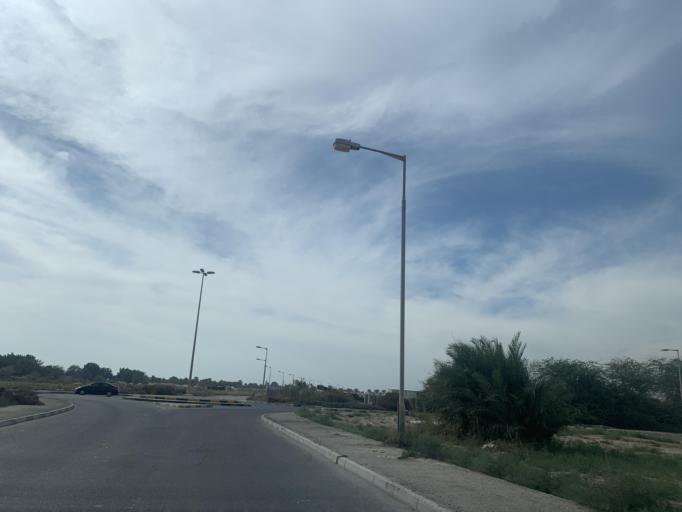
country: BH
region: Central Governorate
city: Madinat Hamad
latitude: 26.1185
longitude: 50.4753
